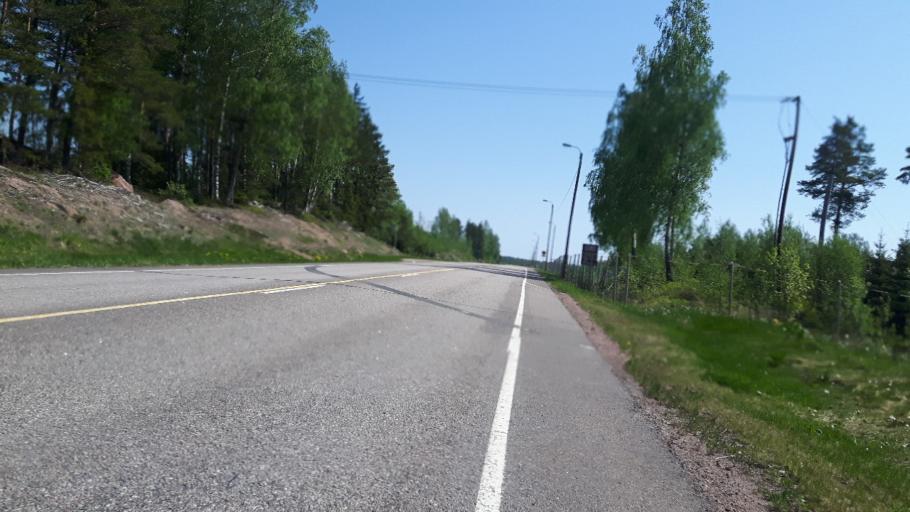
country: FI
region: Uusimaa
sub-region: Loviisa
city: Ruotsinpyhtaeae
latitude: 60.4920
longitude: 26.4551
